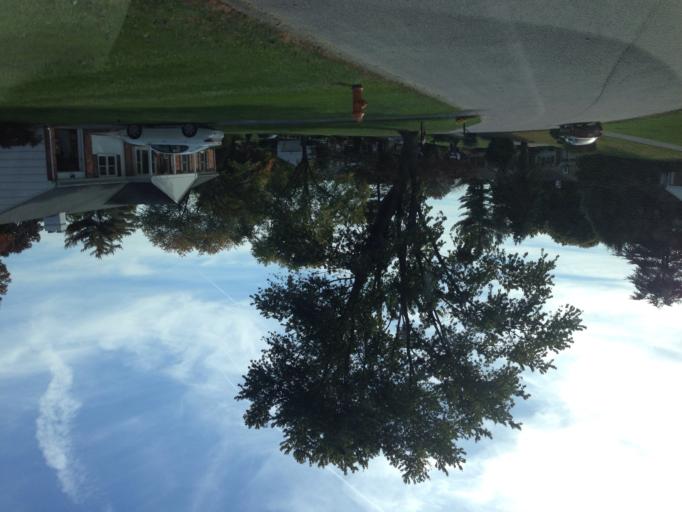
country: US
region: Maryland
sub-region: Howard County
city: Ellicott City
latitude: 39.2826
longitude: -76.8374
